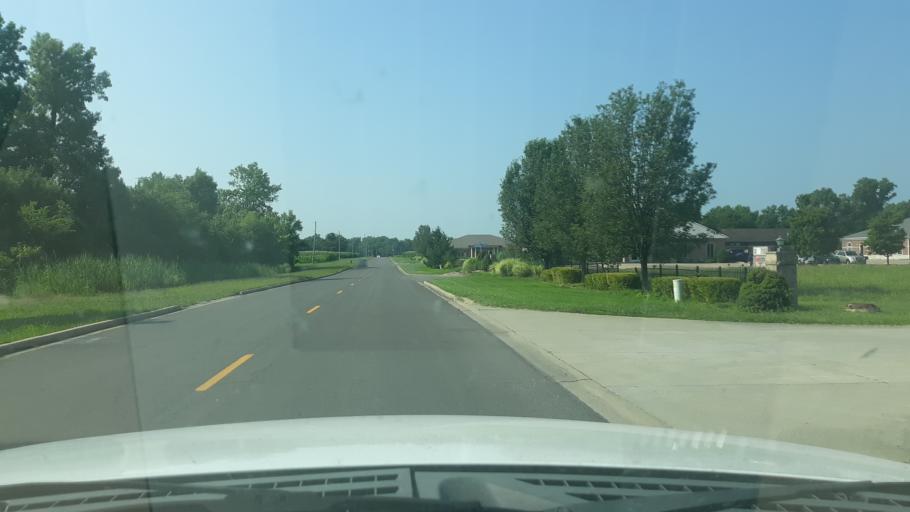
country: US
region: Illinois
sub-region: Williamson County
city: Energy
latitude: 37.7378
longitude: -88.9933
